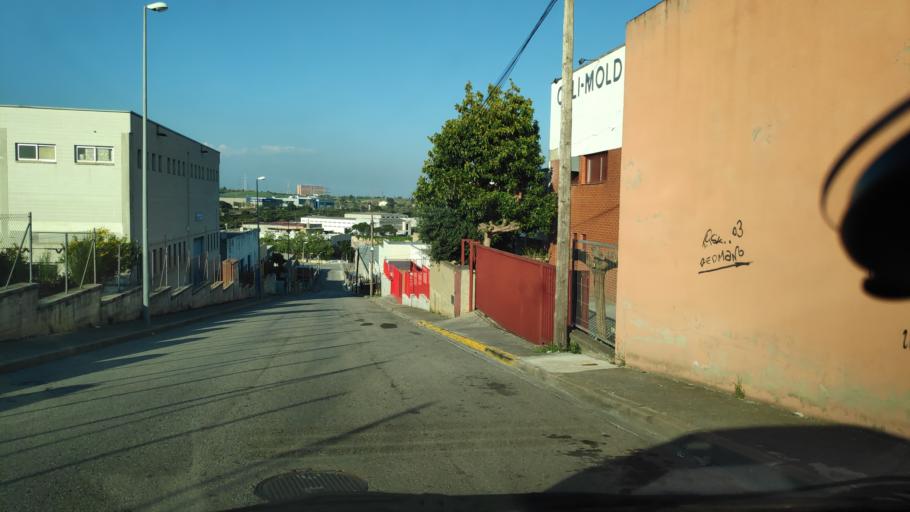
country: ES
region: Catalonia
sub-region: Provincia de Barcelona
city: Terrassa
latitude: 41.5419
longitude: 2.0295
